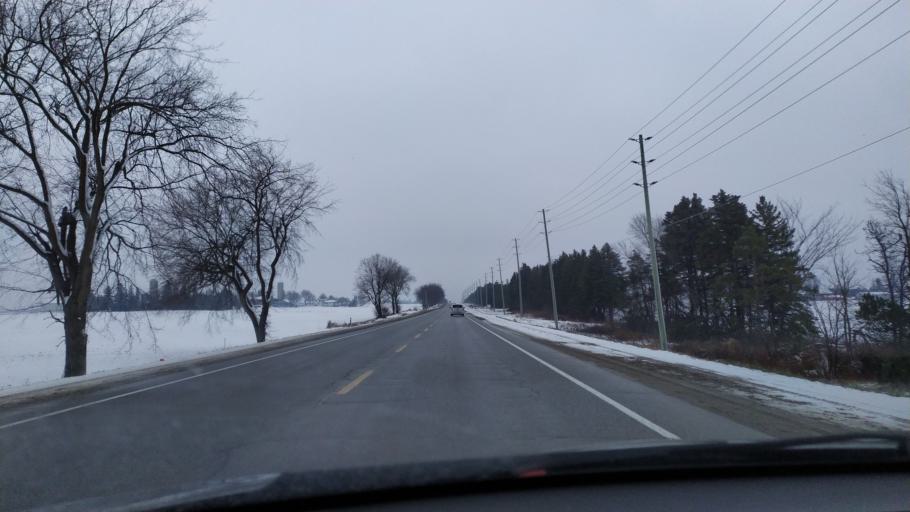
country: CA
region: Ontario
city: Waterloo
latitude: 43.6150
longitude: -80.6727
